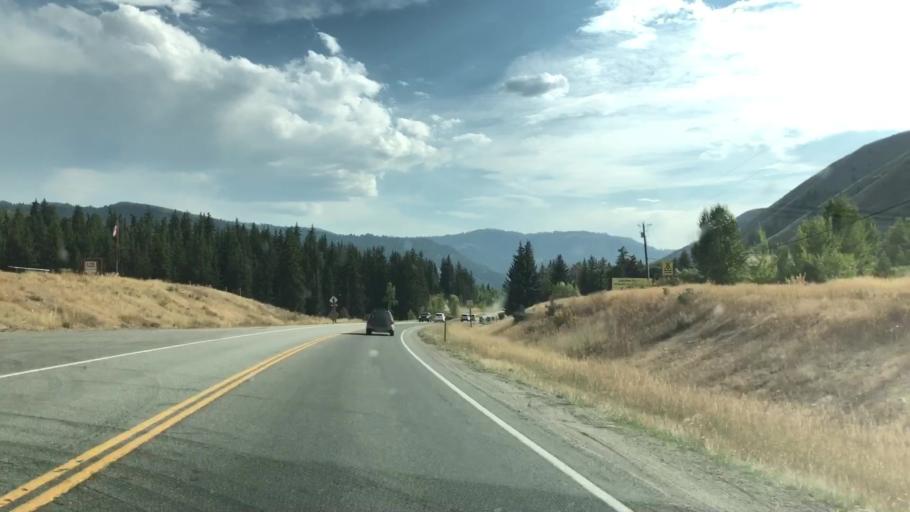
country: US
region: Wyoming
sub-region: Teton County
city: Hoback
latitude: 43.3424
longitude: -110.7224
